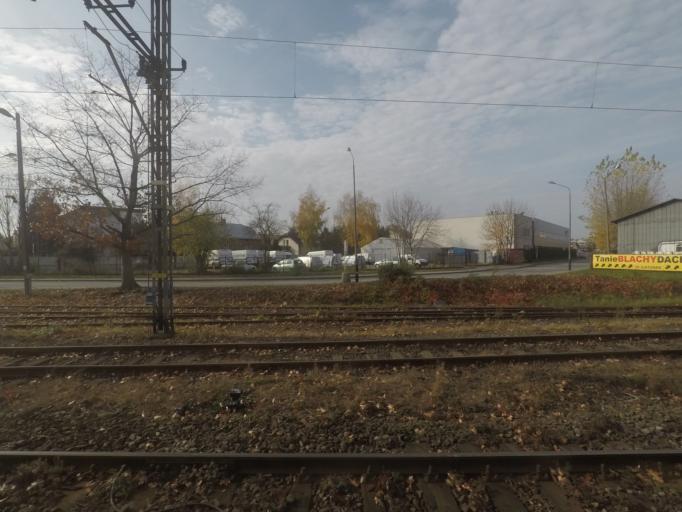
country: PL
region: Subcarpathian Voivodeship
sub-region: Rzeszow
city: Rzeszow
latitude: 50.0461
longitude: 21.9957
